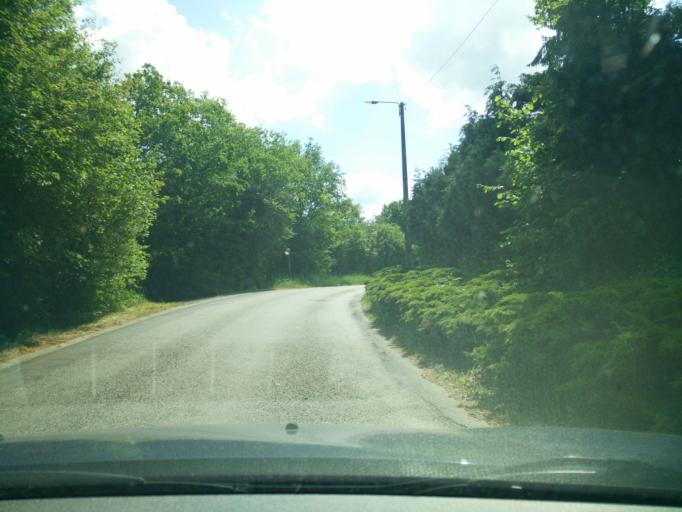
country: BE
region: Wallonia
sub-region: Province de Namur
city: Couvin
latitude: 50.0684
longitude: 4.5148
